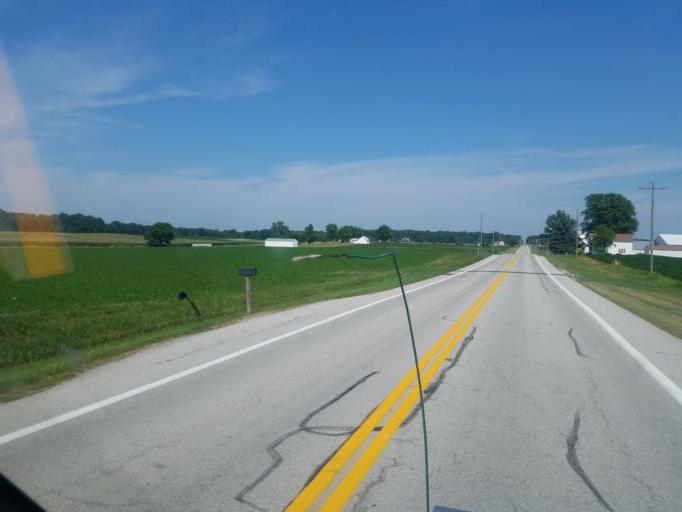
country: US
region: Ohio
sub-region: Shelby County
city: Botkins
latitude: 40.4968
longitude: -84.1981
